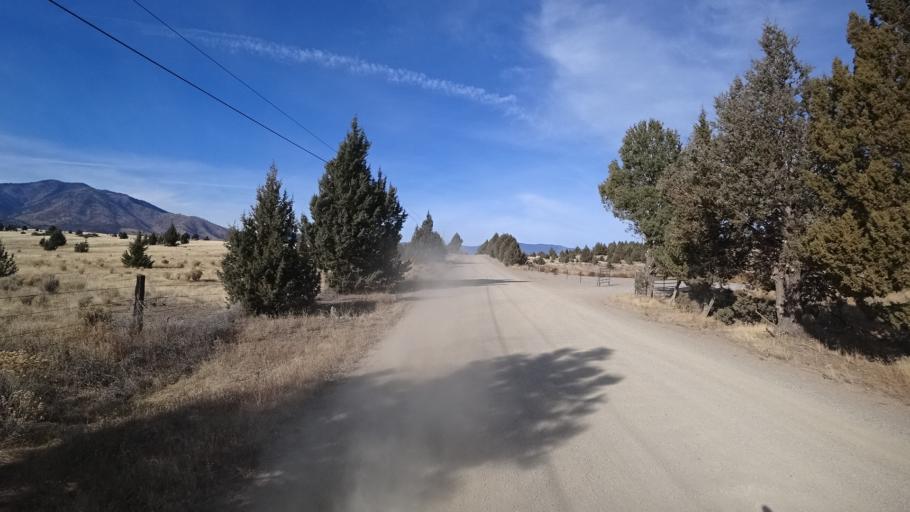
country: US
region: California
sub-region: Siskiyou County
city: Weed
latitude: 41.4882
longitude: -122.4460
